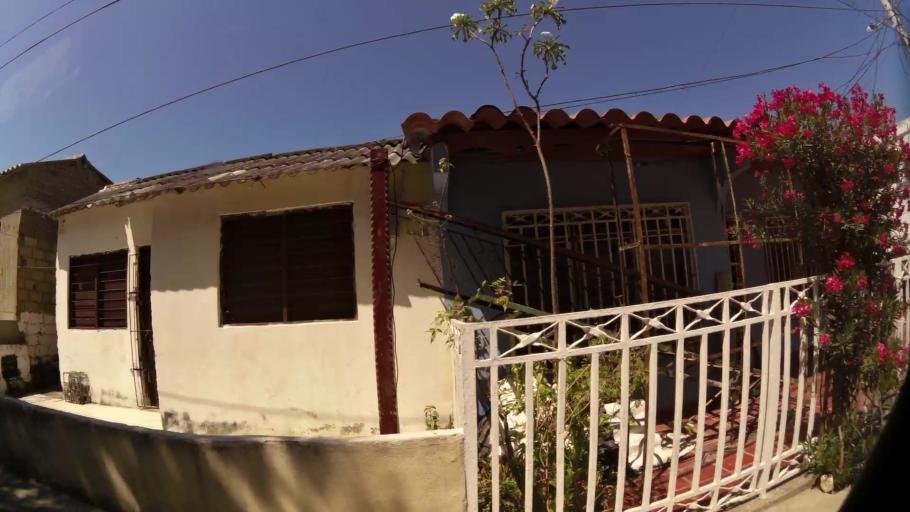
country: CO
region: Bolivar
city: Cartagena
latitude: 10.4314
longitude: -75.5284
